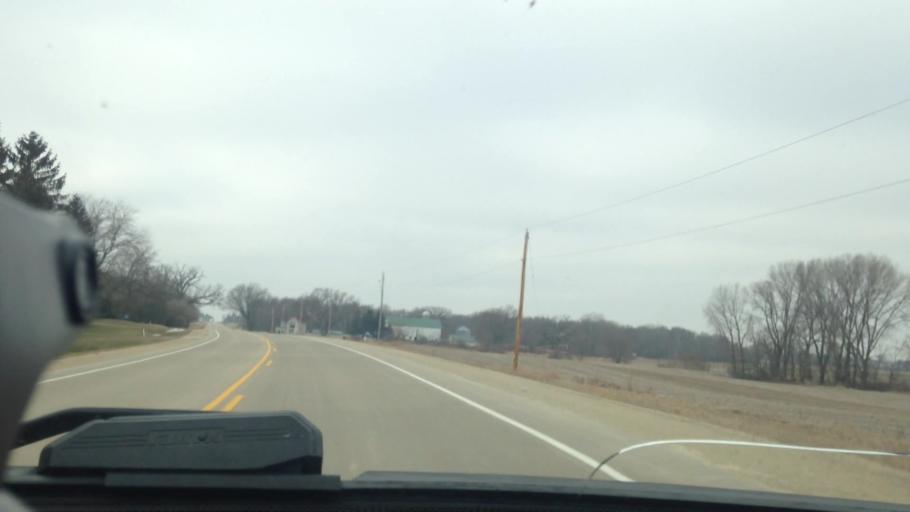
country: US
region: Wisconsin
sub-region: Dodge County
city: Horicon
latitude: 43.4734
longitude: -88.6866
